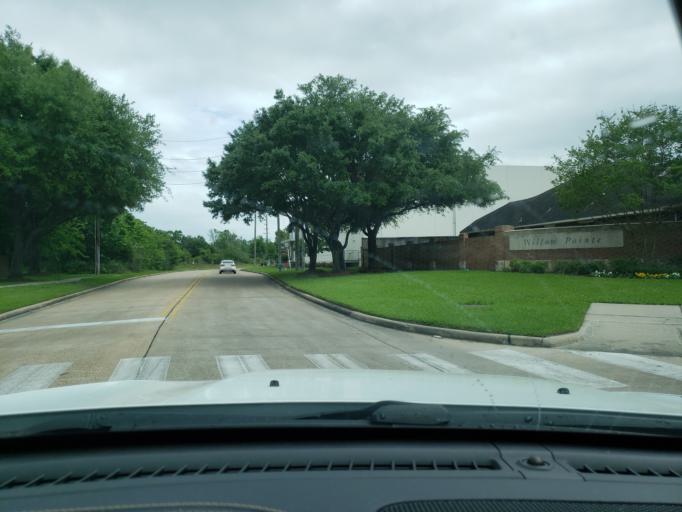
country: US
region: Texas
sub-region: Harris County
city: Jersey Village
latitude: 29.9194
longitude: -95.5636
